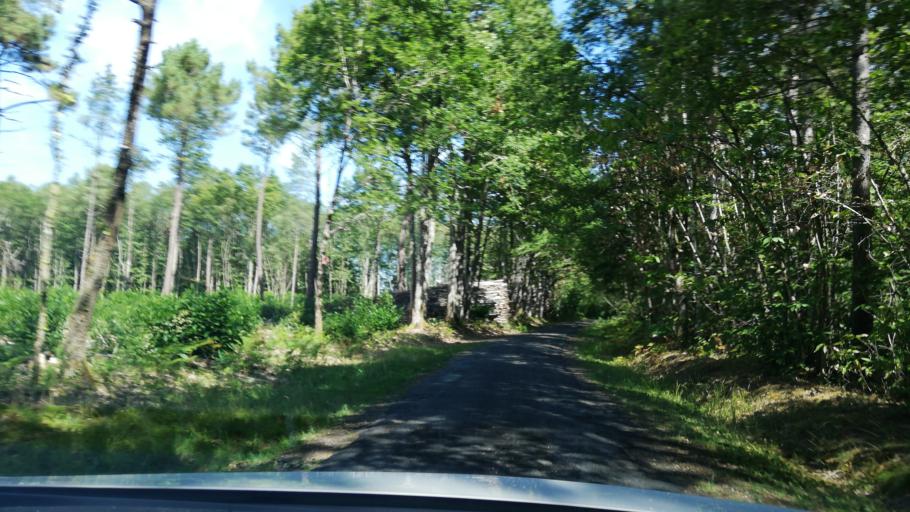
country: FR
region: Centre
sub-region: Departement d'Indre-et-Loire
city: Mazieres-de-Touraine
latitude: 47.3754
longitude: 0.4310
